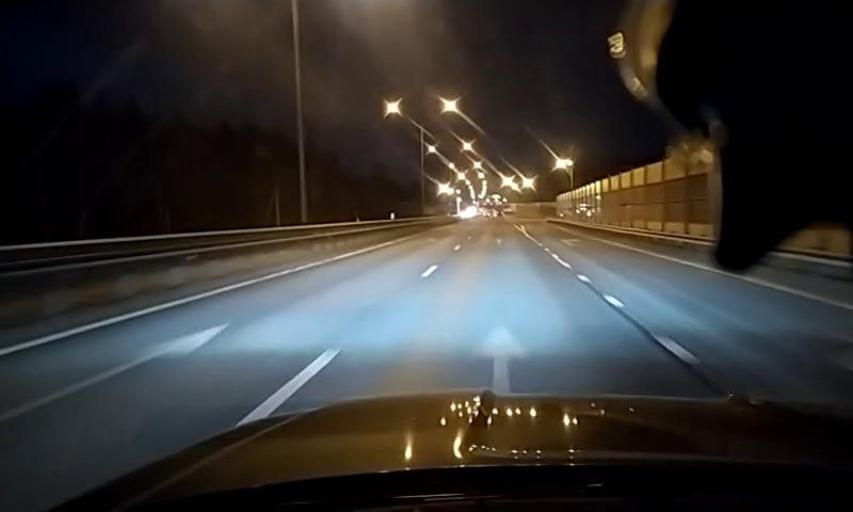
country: RU
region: Leningrad
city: Agalatovo
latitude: 60.2289
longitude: 30.3579
